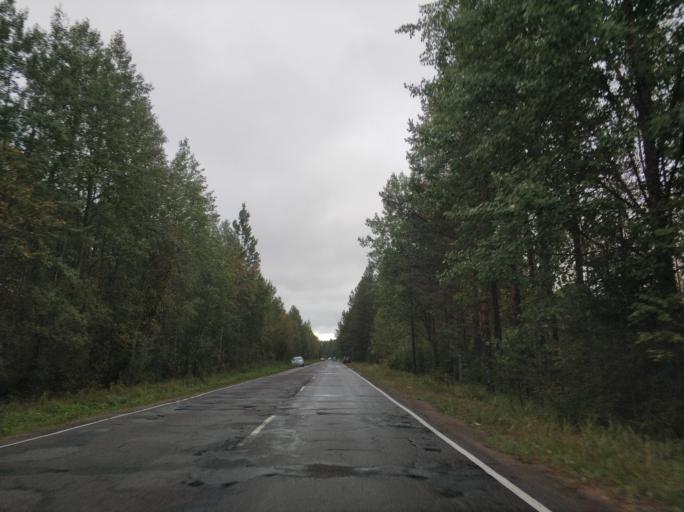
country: RU
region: Leningrad
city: Borisova Griva
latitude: 60.1685
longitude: 30.9204
